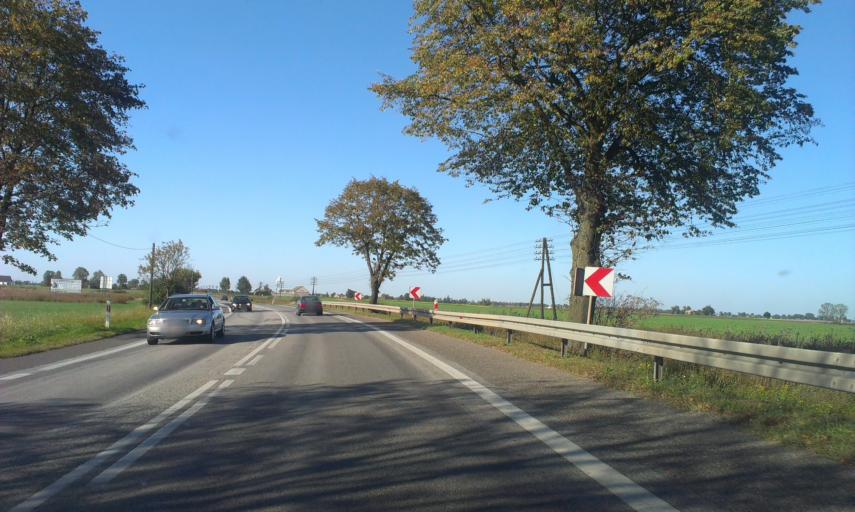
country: PL
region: Kujawsko-Pomorskie
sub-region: Powiat torunski
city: Lysomice
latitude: 53.1244
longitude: 18.6273
